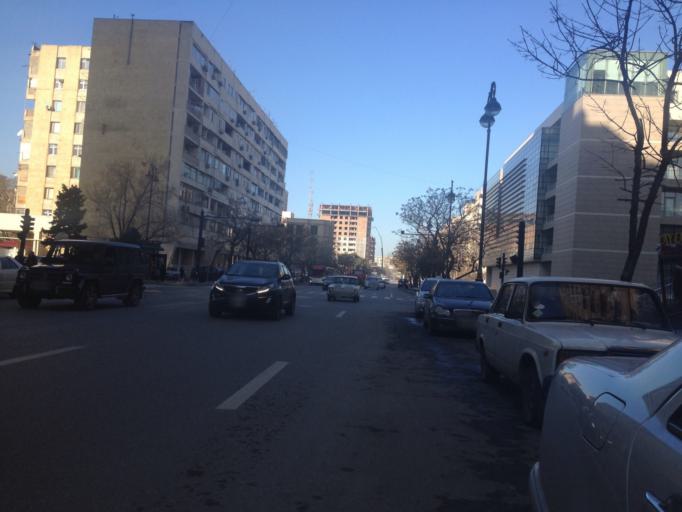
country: AZ
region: Baki
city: Baku
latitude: 40.3977
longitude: 49.8392
